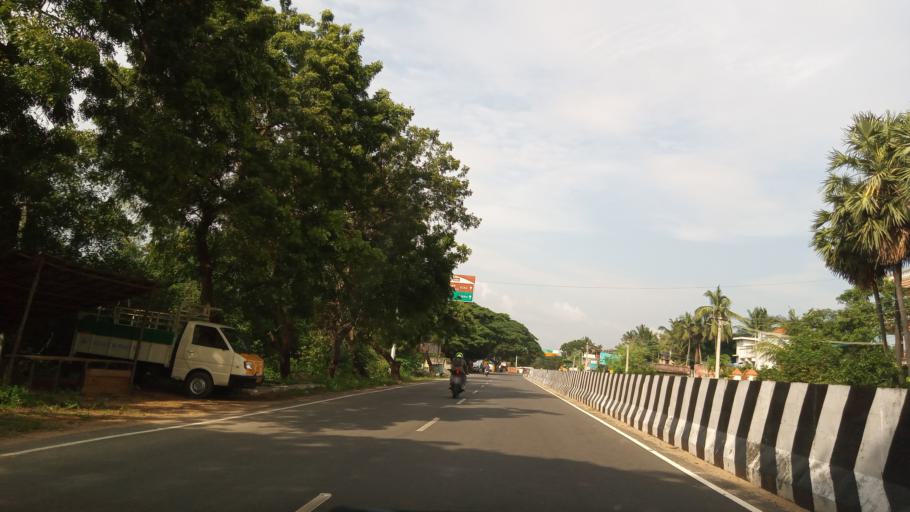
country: IN
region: Tamil Nadu
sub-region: Villupuram
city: Auroville
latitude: 12.0545
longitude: 79.8735
